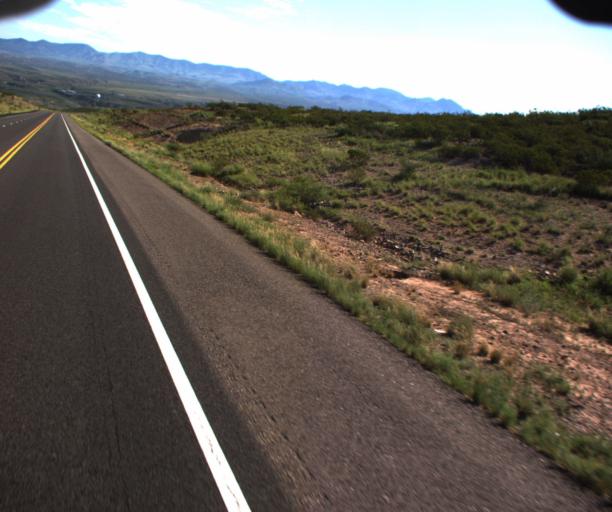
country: US
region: Arizona
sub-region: Greenlee County
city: Clifton
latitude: 32.9186
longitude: -109.2483
